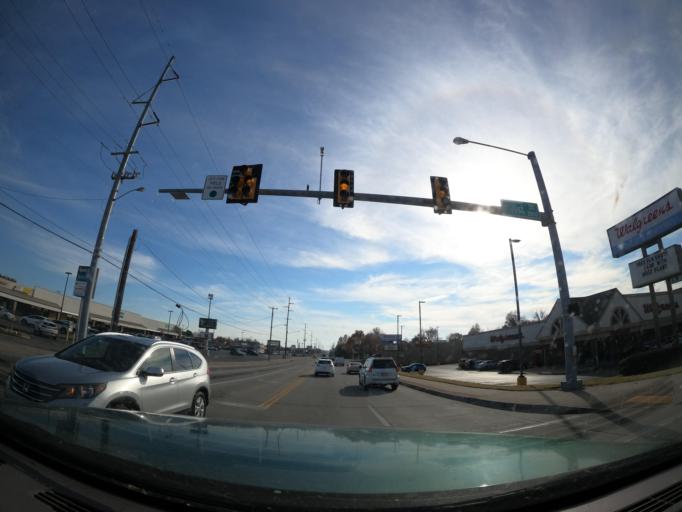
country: US
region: Oklahoma
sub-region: Tulsa County
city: Tulsa
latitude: 36.1187
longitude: -95.9403
